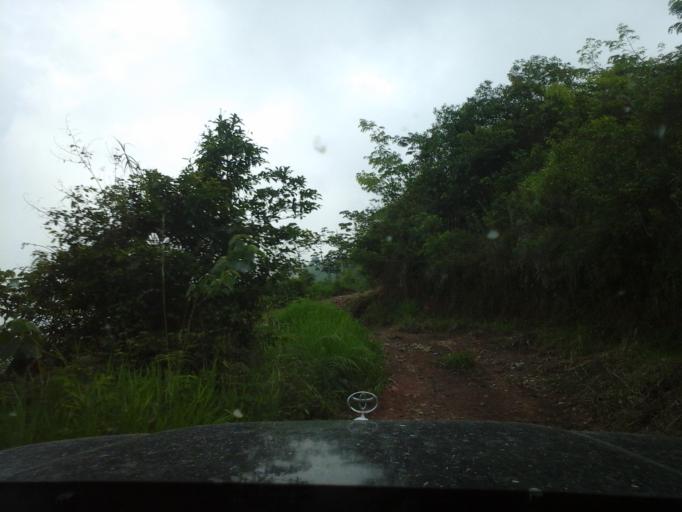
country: CO
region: Cesar
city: Agustin Codazzi
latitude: 9.9542
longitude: -73.0665
